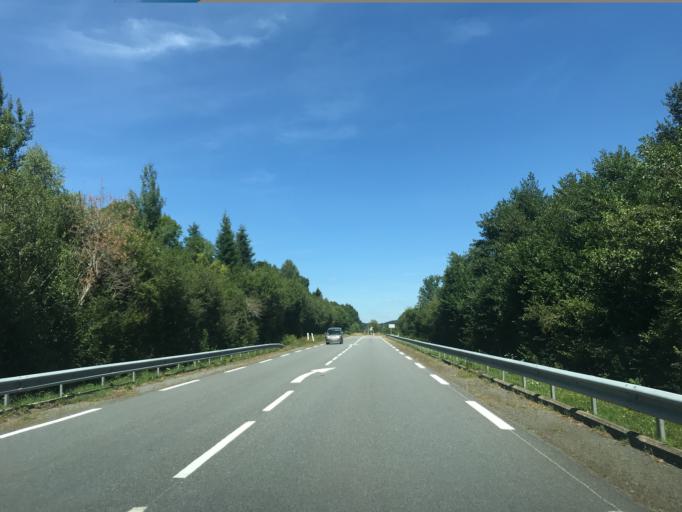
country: FR
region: Limousin
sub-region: Departement de la Creuse
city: Felletin
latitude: 45.8106
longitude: 2.1558
